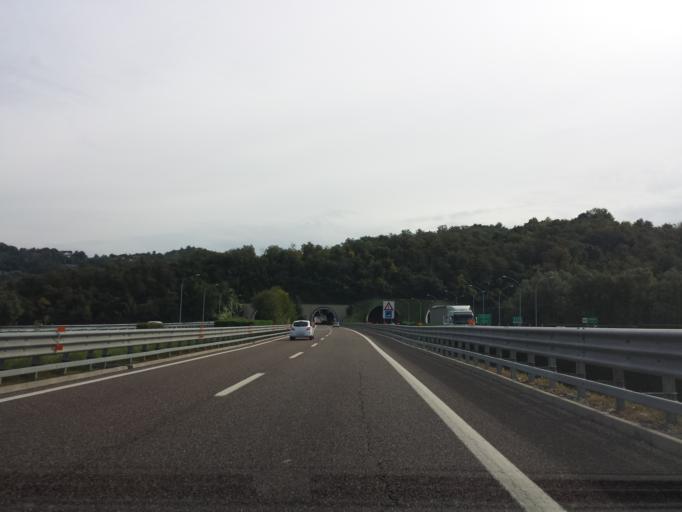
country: IT
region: Veneto
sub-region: Provincia di Vicenza
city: Arcugnano-Torri
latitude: 45.5176
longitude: 11.5297
